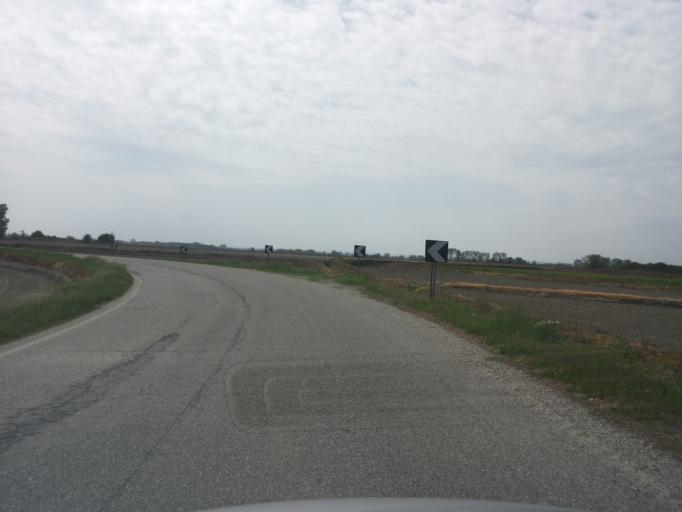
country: IT
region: Piedmont
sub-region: Provincia di Vercelli
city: Caresana
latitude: 45.2127
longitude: 8.5051
